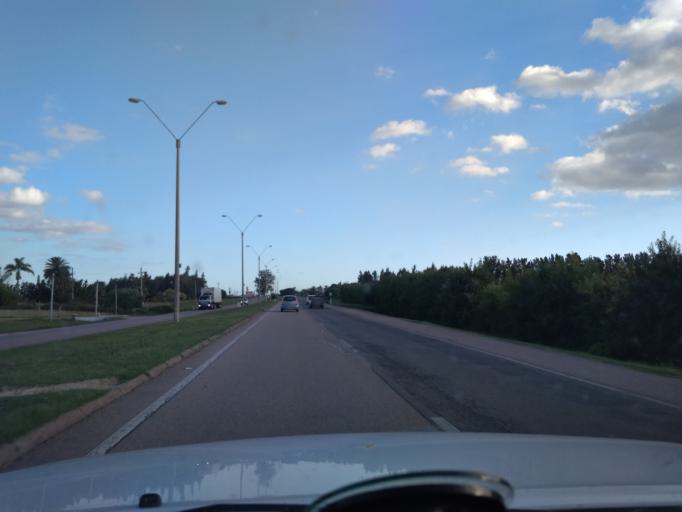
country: UY
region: Canelones
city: Joanico
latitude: -34.6086
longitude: -56.2604
